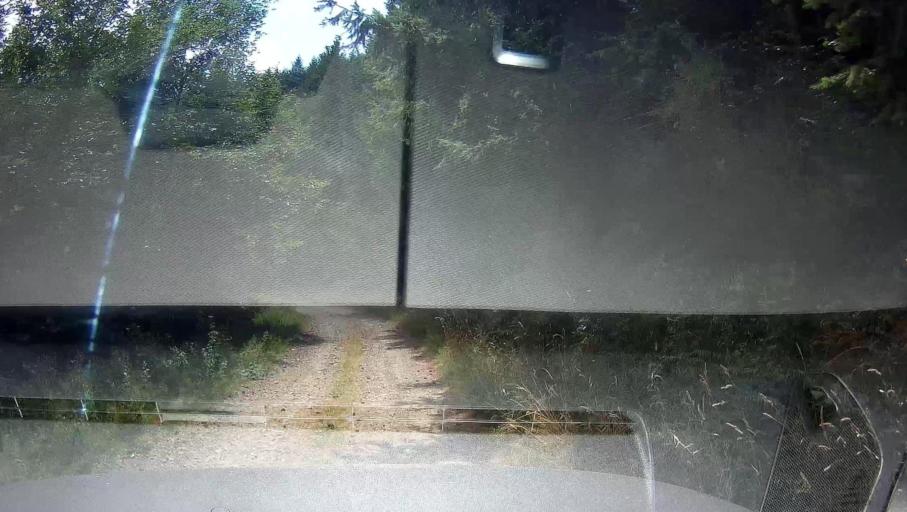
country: FR
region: Rhone-Alpes
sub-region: Departement du Rhone
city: Grandris
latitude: 46.0232
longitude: 4.5418
